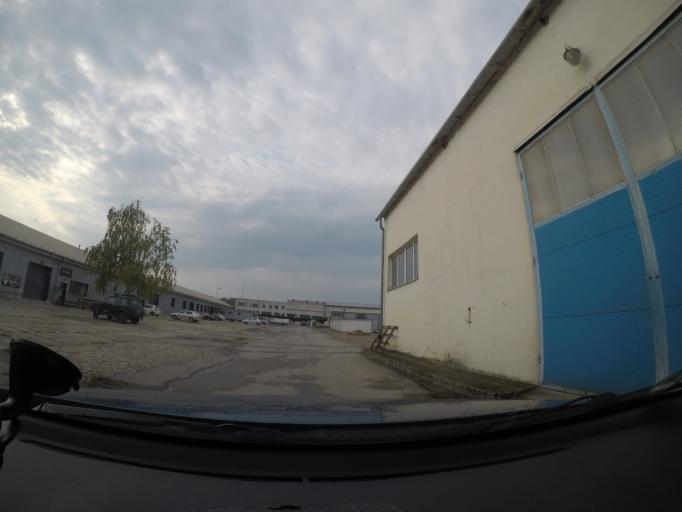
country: SK
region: Trenciansky
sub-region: Okres Trencin
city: Trencin
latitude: 48.8906
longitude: 18.0164
